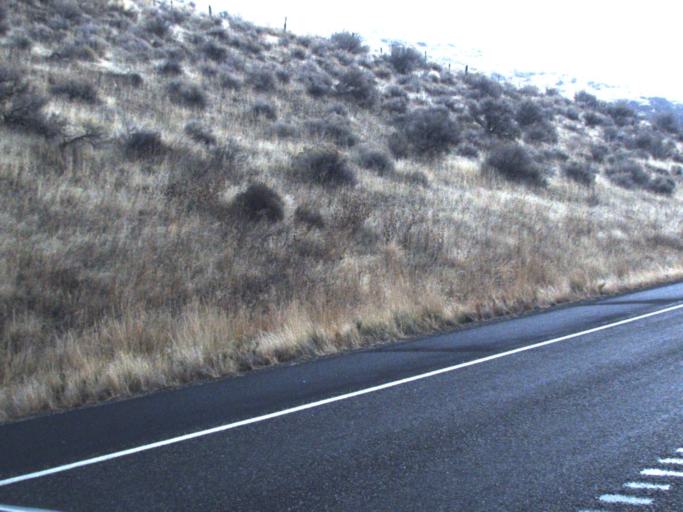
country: US
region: Washington
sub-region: Asotin County
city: Clarkston Heights-Vineland
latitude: 46.4097
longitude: -117.2664
